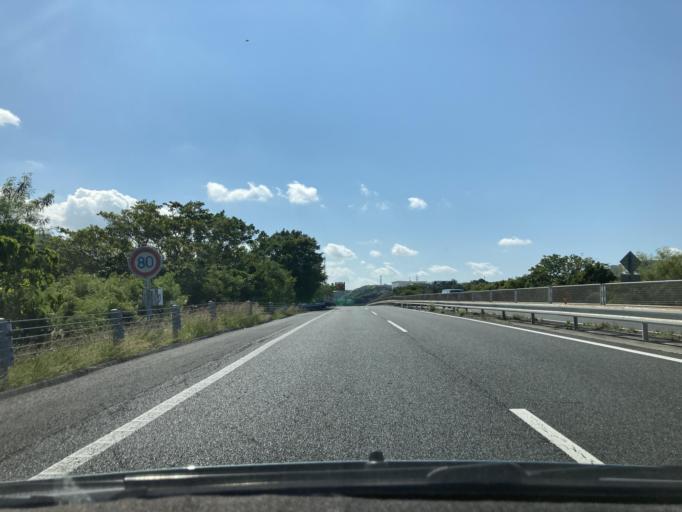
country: JP
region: Okinawa
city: Ginowan
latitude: 26.2314
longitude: 127.7392
